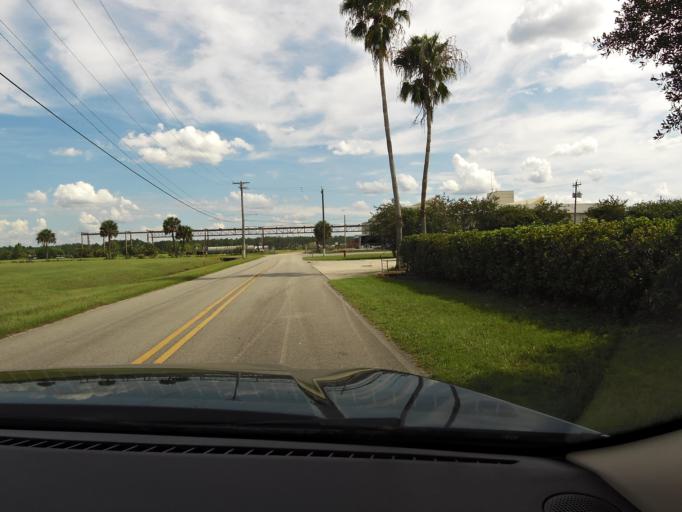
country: US
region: Florida
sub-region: Clay County
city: Green Cove Springs
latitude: 29.9790
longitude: -81.6563
